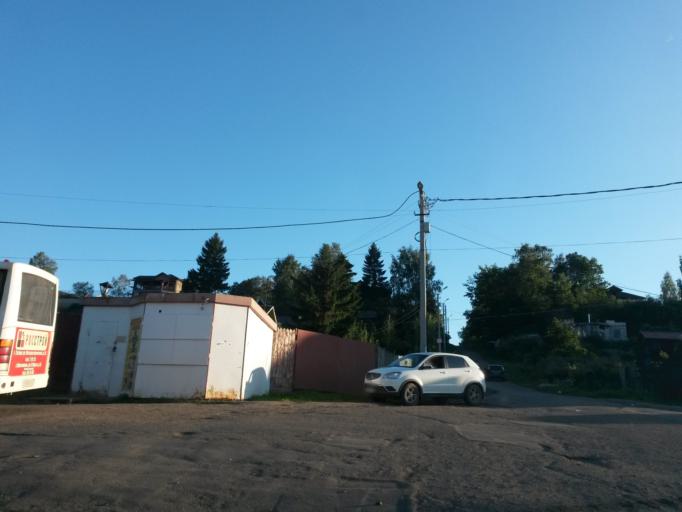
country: RU
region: Jaroslavl
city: Tutayev
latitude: 57.8736
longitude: 39.5355
